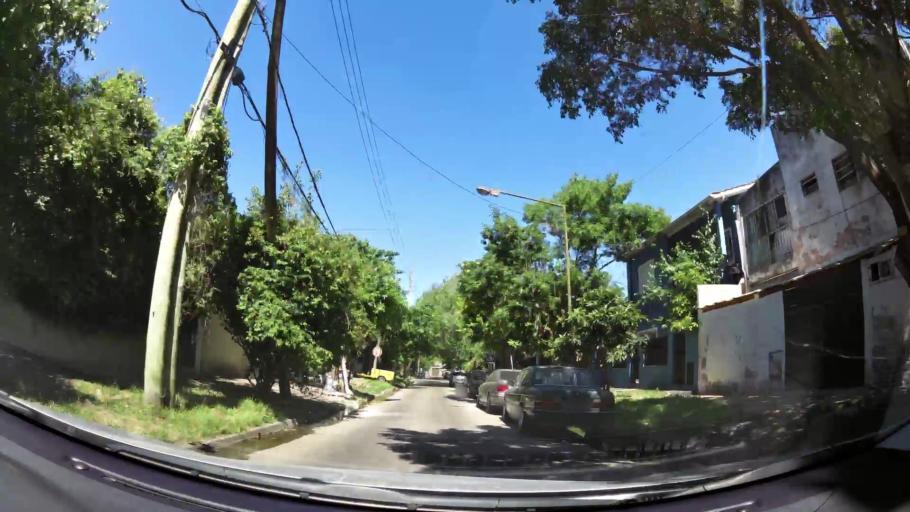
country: AR
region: Buenos Aires
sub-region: Partido de San Isidro
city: San Isidro
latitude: -34.4636
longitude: -58.5060
